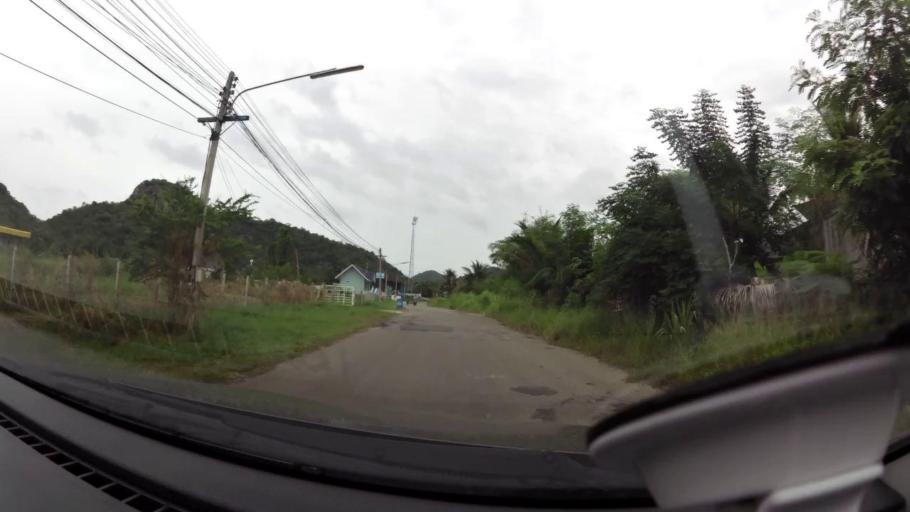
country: TH
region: Prachuap Khiri Khan
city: Pran Buri
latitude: 12.4489
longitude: 99.9712
